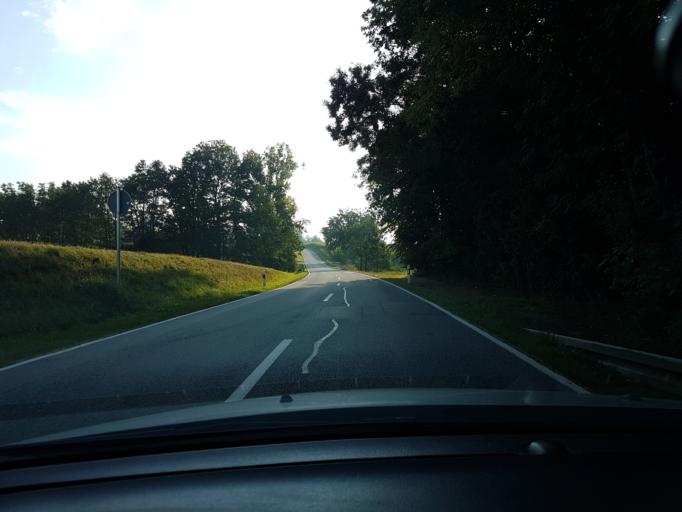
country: DE
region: Bavaria
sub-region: Lower Bavaria
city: Geisenhausen
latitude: 48.4888
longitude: 12.3122
